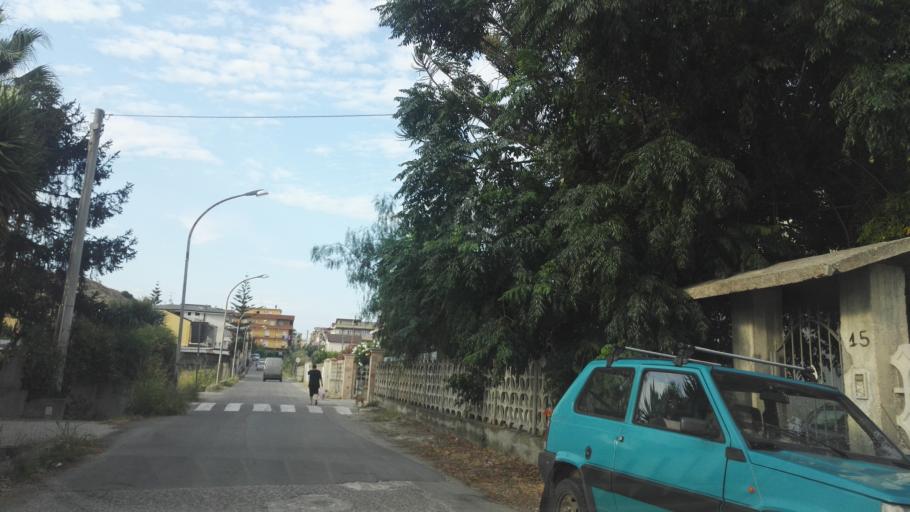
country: IT
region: Calabria
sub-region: Provincia di Reggio Calabria
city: Monasterace Marina
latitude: 38.4325
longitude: 16.5697
